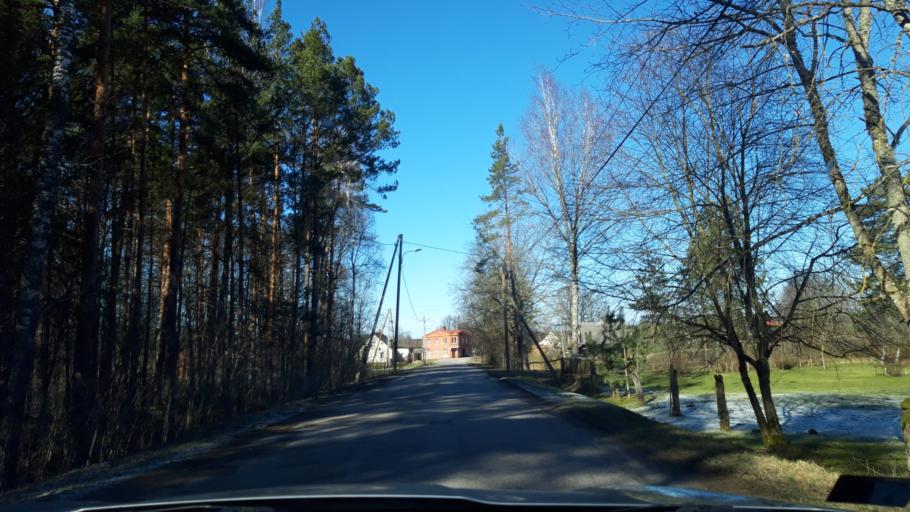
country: LV
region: Strenci
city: Strenci
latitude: 57.6227
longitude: 25.6961
